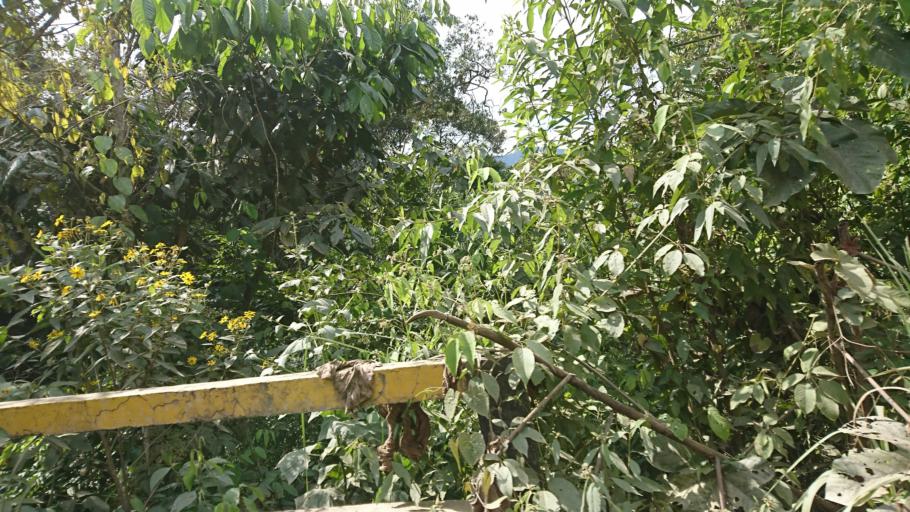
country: BO
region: La Paz
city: Coroico
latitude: -16.0847
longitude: -67.7902
